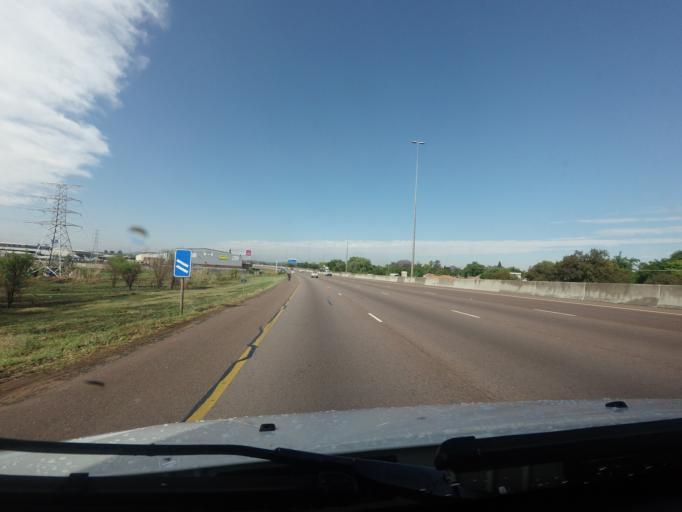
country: ZA
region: Gauteng
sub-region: City of Tshwane Metropolitan Municipality
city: Pretoria
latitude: -25.7054
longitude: 28.2686
